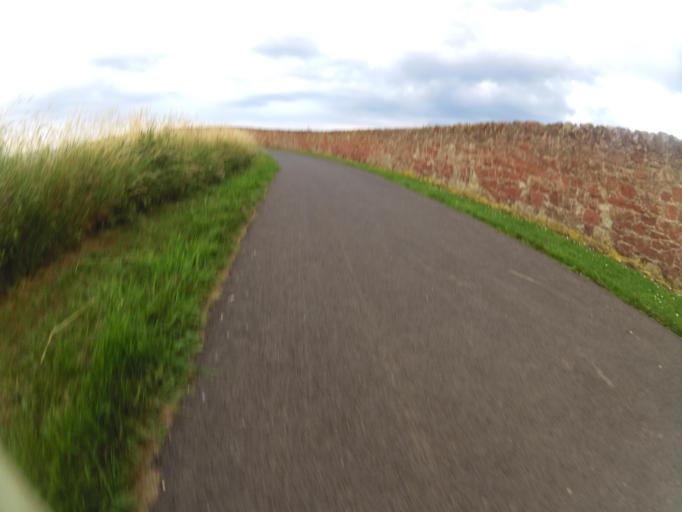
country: GB
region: Scotland
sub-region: East Lothian
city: Dunbar
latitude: 56.0052
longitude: -2.5341
